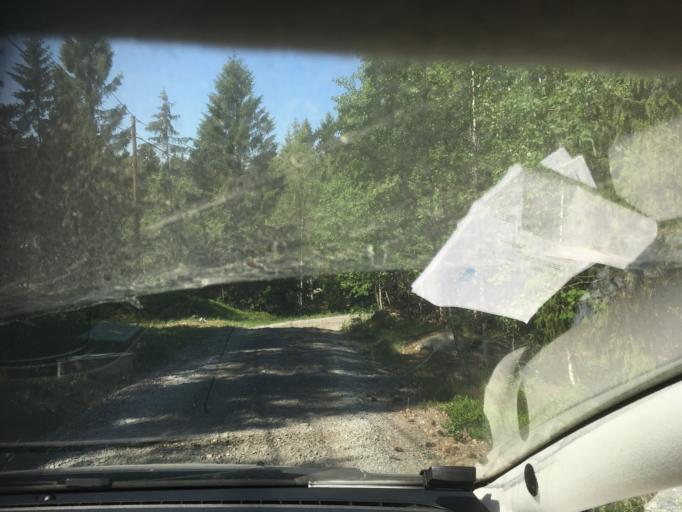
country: SE
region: Stockholm
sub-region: Haninge Kommun
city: Jordbro
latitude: 59.0110
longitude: 18.1639
